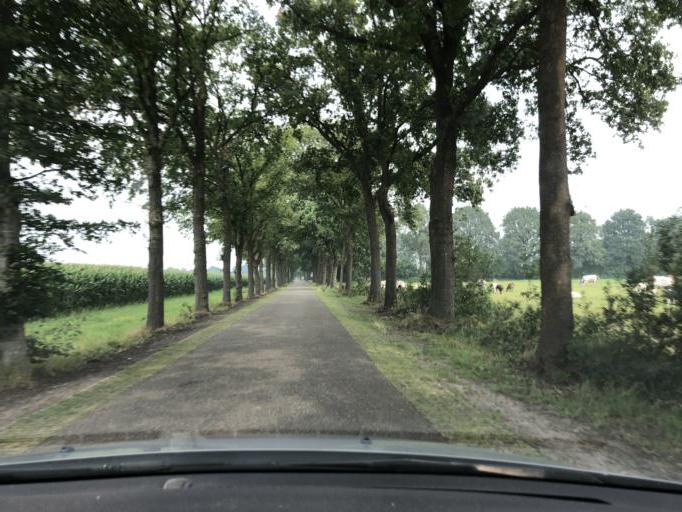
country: NL
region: Overijssel
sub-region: Gemeente Dalfsen
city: Dalfsen
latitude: 52.5830
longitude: 6.2964
